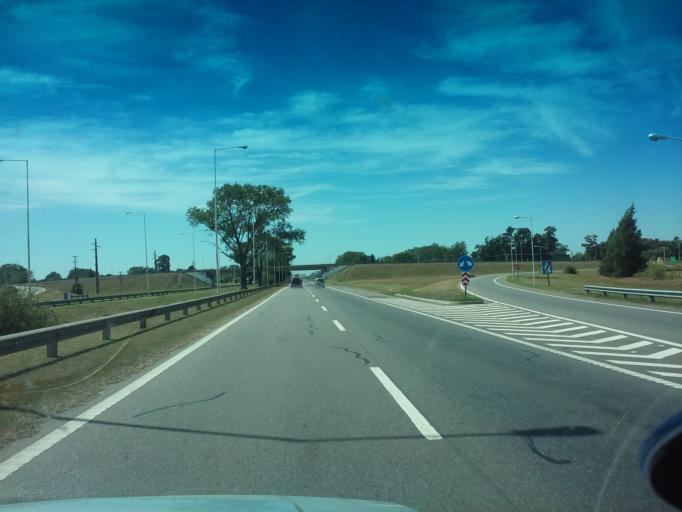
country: AR
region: Buenos Aires
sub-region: Partido de Mercedes
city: Mercedes
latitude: -34.6570
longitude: -59.3575
